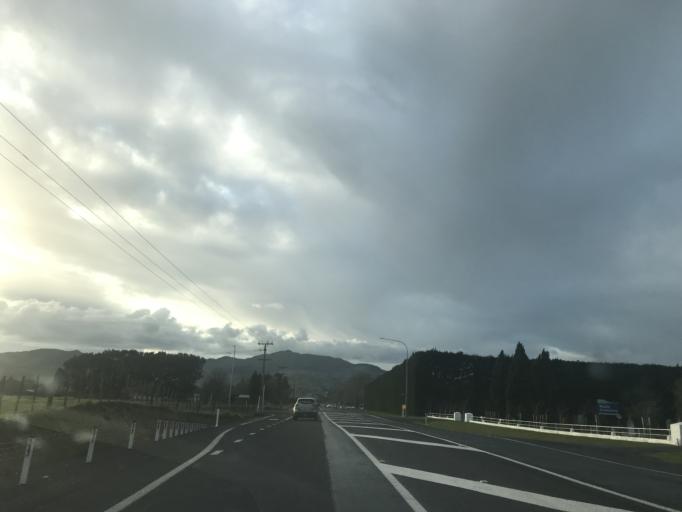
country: NZ
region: Waikato
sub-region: Hauraki District
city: Waihi
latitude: -37.4102
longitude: 175.8620
